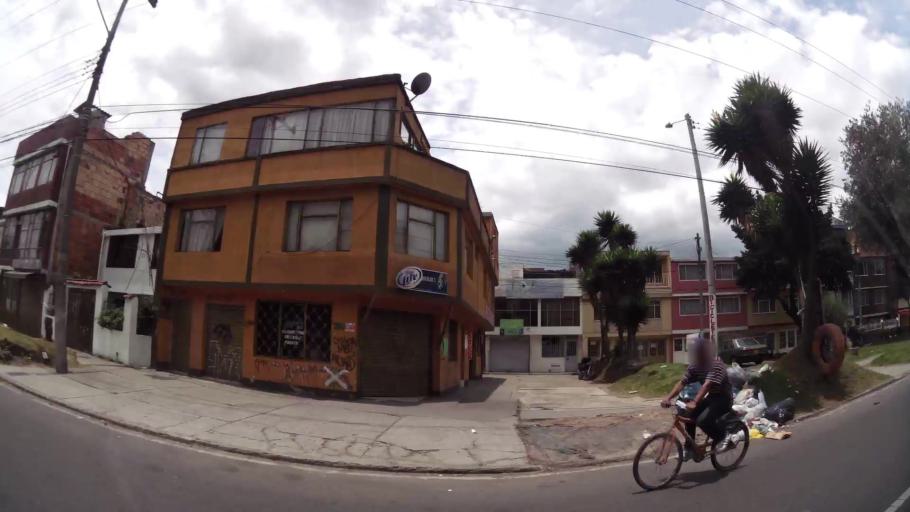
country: CO
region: Cundinamarca
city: Funza
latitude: 4.7146
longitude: -74.1176
